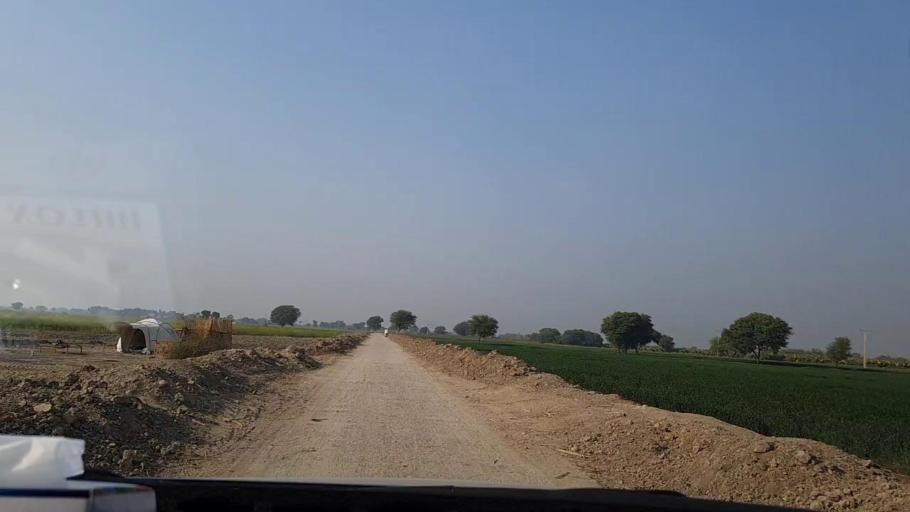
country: PK
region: Sindh
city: Tando Ghulam Ali
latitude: 25.2011
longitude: 68.8741
